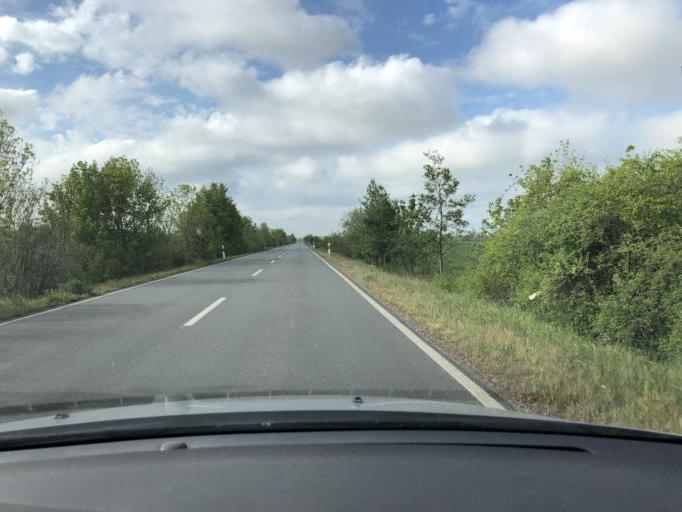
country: DE
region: Saxony
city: Neukieritzsch
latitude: 51.1744
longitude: 12.4188
